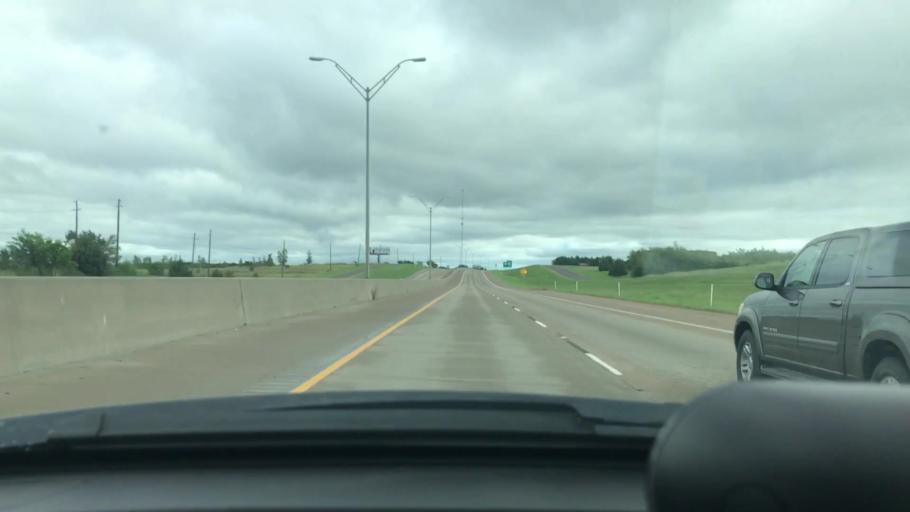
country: US
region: Texas
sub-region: Grayson County
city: Howe
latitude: 33.5180
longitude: -96.6154
